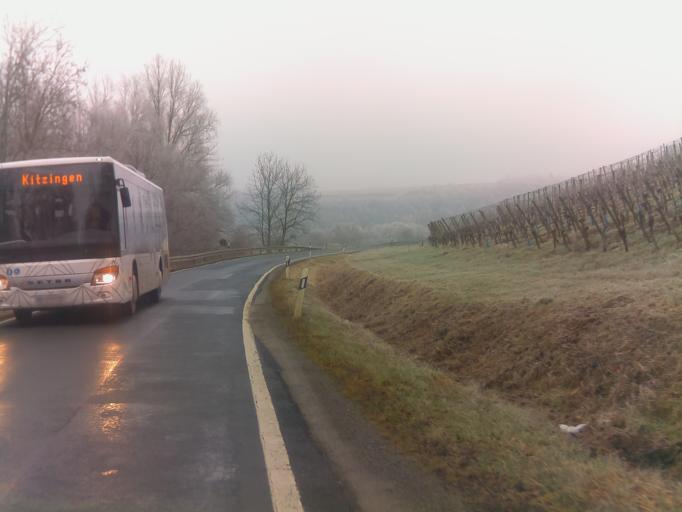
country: DE
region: Bavaria
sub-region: Regierungsbezirk Unterfranken
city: Segnitz
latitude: 49.6835
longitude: 10.1391
